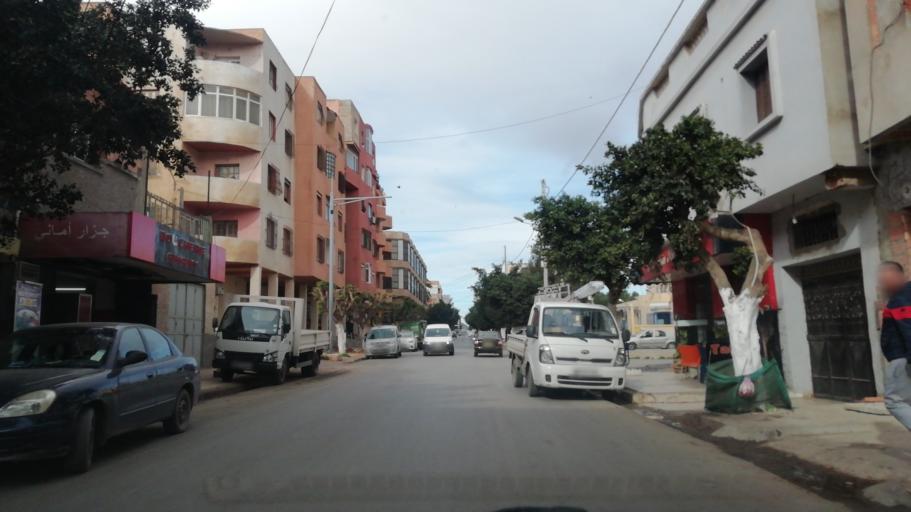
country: DZ
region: Oran
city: Oran
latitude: 35.6851
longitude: -0.6163
